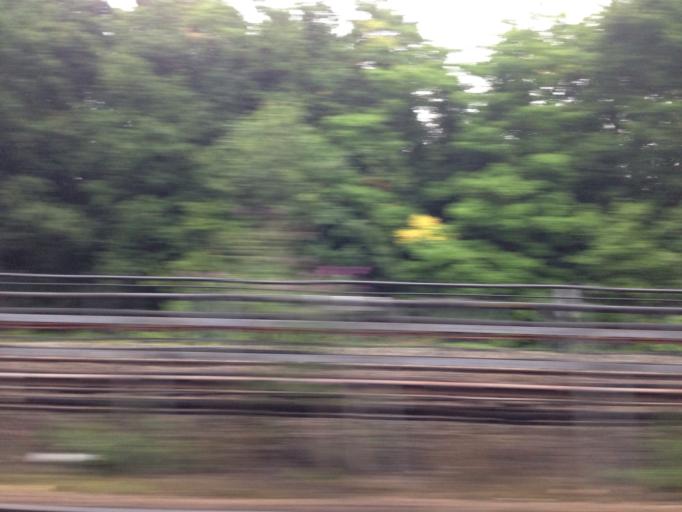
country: GB
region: England
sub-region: Greater London
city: Ealing Broadway
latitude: 51.5301
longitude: -0.2917
